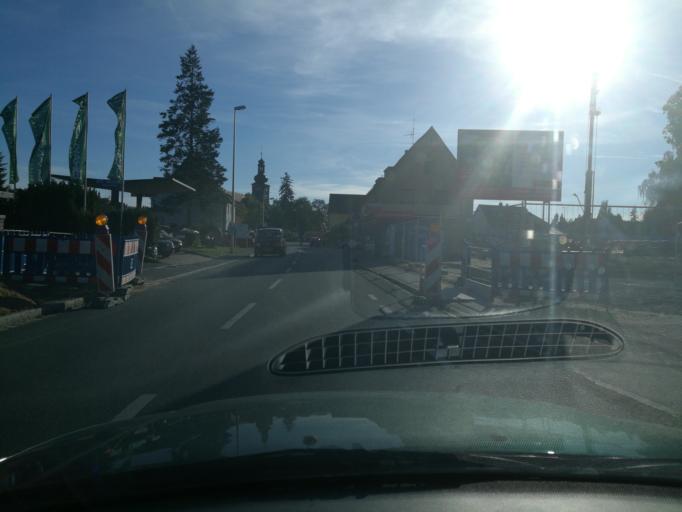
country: DE
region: Bavaria
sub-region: Regierungsbezirk Mittelfranken
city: Erlangen
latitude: 49.5694
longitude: 10.9629
